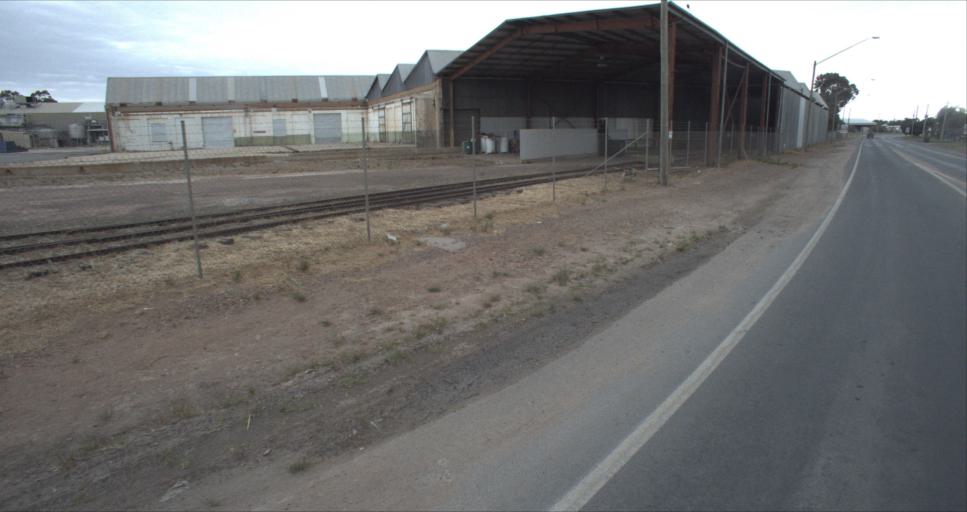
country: AU
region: New South Wales
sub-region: Leeton
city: Leeton
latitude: -34.5499
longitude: 146.3950
